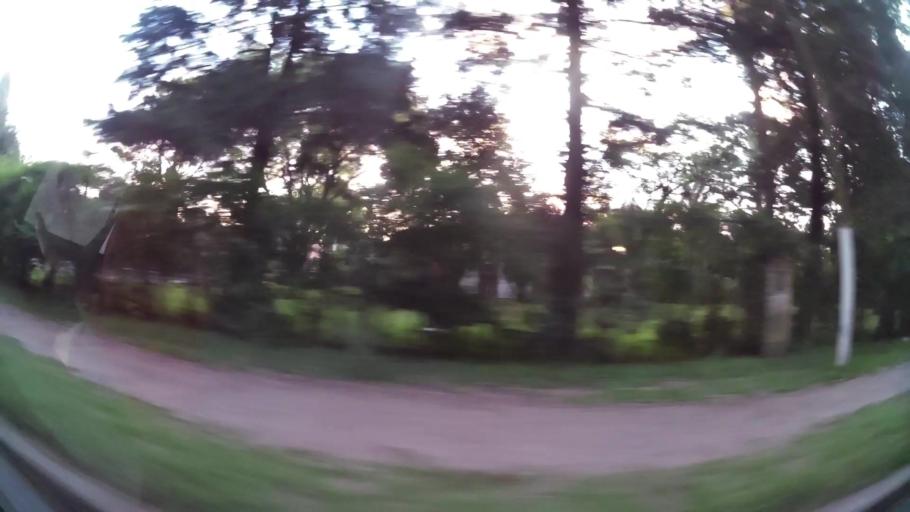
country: AR
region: Buenos Aires
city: Santa Catalina - Dique Lujan
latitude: -34.4857
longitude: -58.7775
